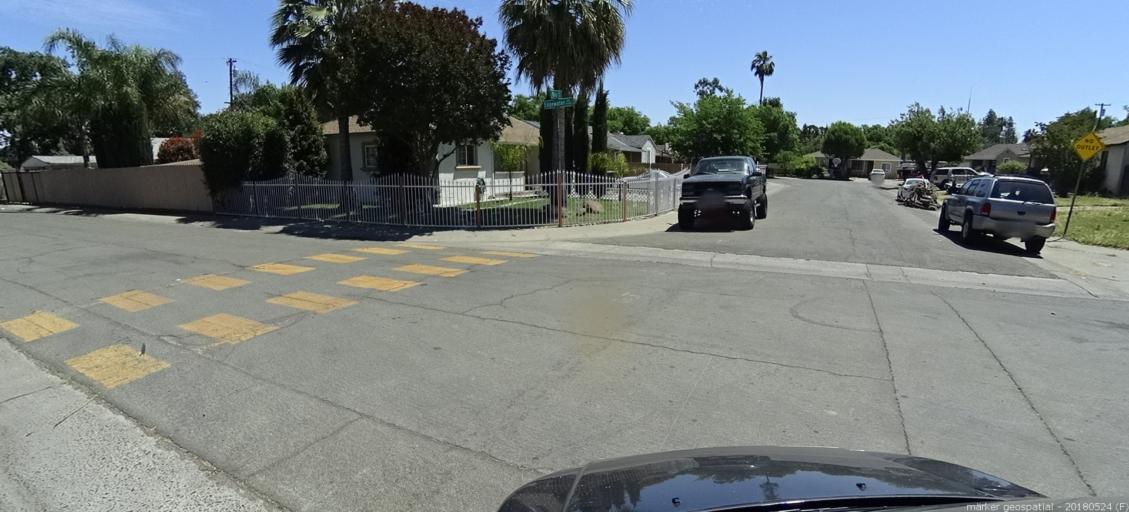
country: US
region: California
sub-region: Sacramento County
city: Sacramento
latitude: 38.6131
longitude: -121.4619
